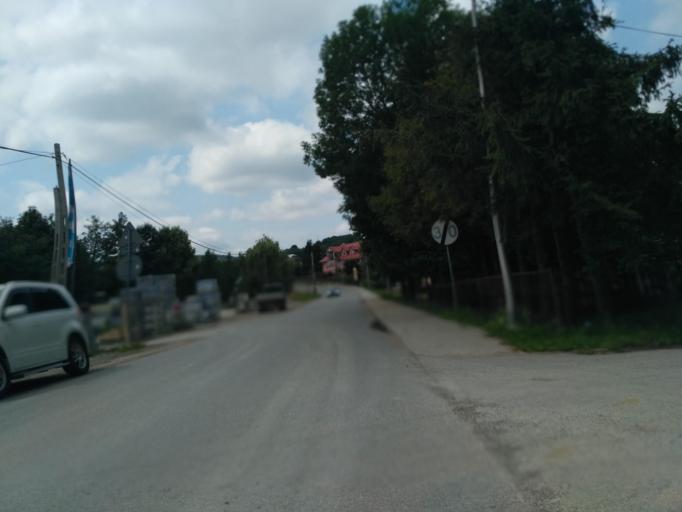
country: PL
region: Subcarpathian Voivodeship
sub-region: Powiat krosnienski
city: Rymanow
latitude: 49.5877
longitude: 21.8271
